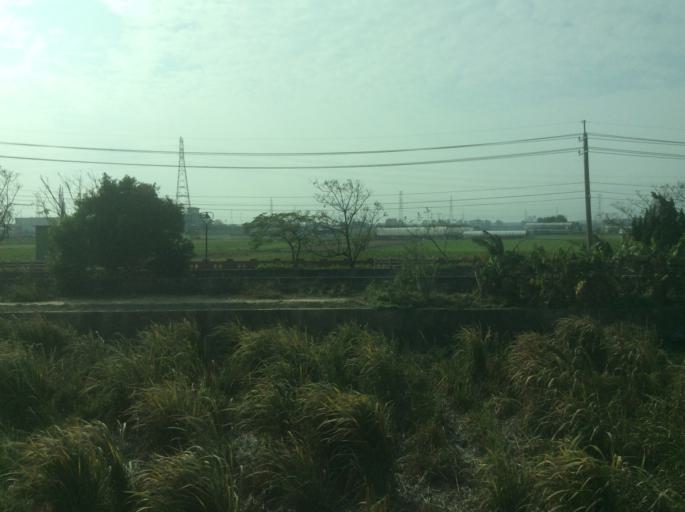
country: TW
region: Taiwan
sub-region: Changhua
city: Chang-hua
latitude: 24.1469
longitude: 120.5438
